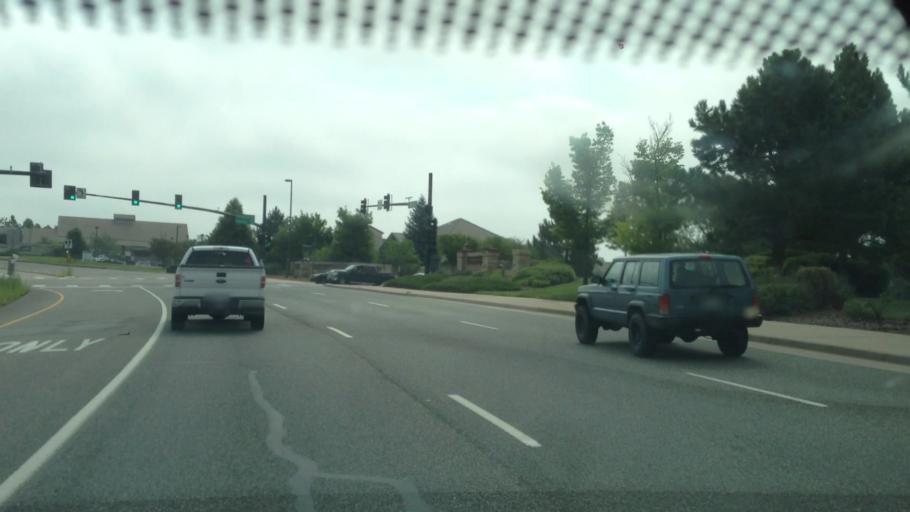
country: US
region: Colorado
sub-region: Douglas County
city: Parker
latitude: 39.6011
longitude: -104.7236
